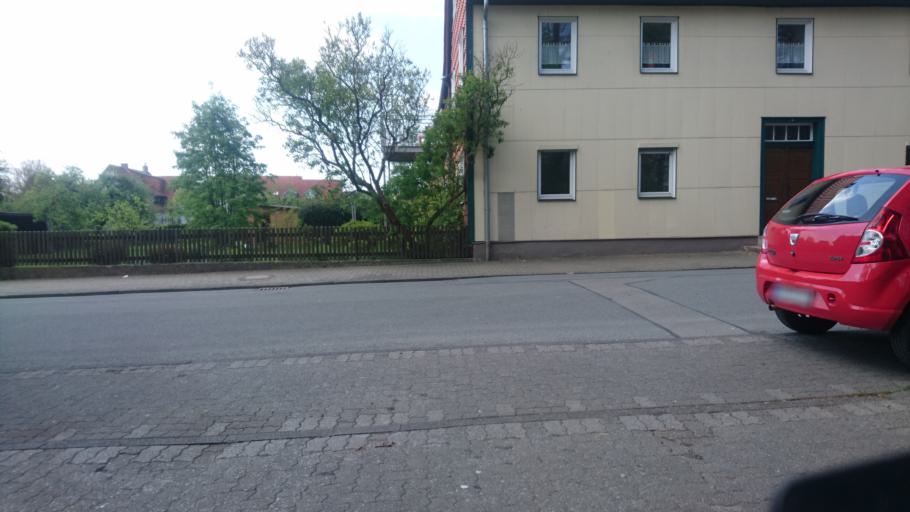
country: DE
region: Hesse
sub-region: Regierungsbezirk Kassel
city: Bad Arolsen
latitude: 51.3777
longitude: 9.0182
